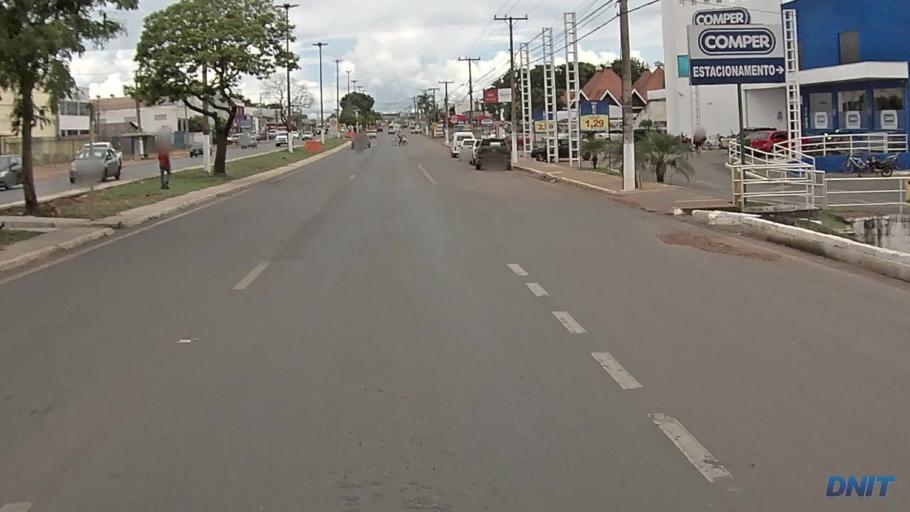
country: BR
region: Mato Grosso
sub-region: Varzea Grande
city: Varzea Grande
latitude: -15.6408
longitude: -56.1726
